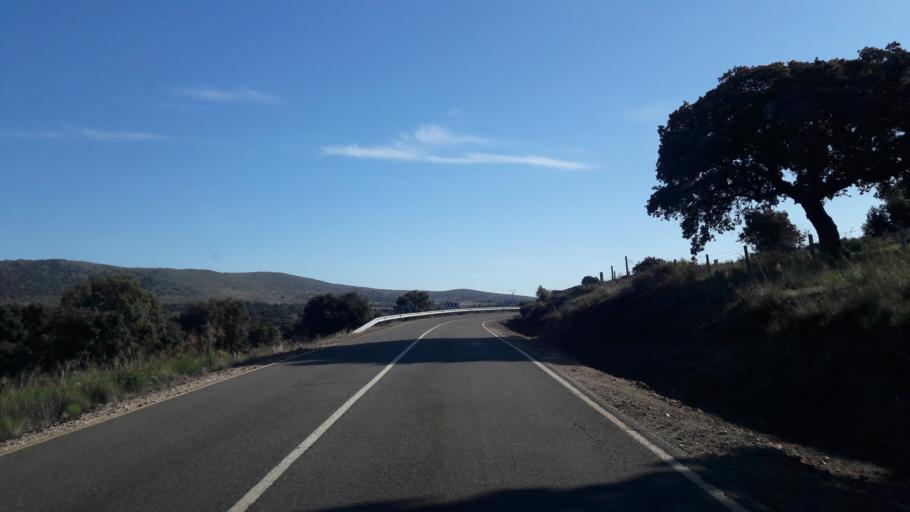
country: ES
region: Castille and Leon
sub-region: Provincia de Avila
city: Narrillos del Alamo
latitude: 40.5263
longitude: -5.4859
